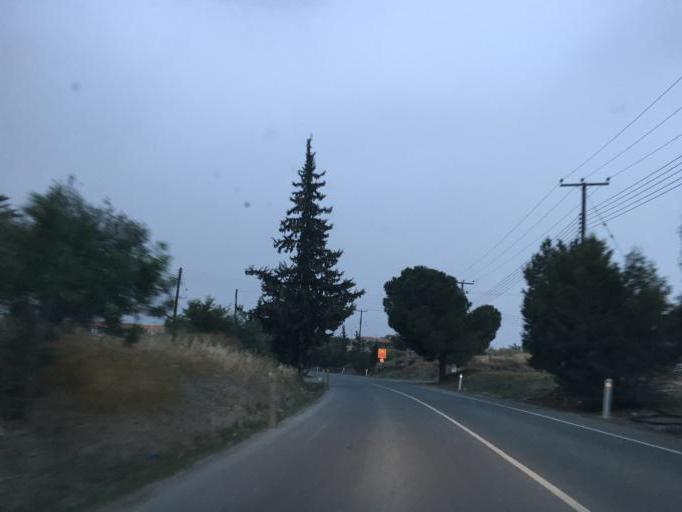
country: CY
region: Limassol
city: Parekklisha
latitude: 34.7420
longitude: 33.1555
